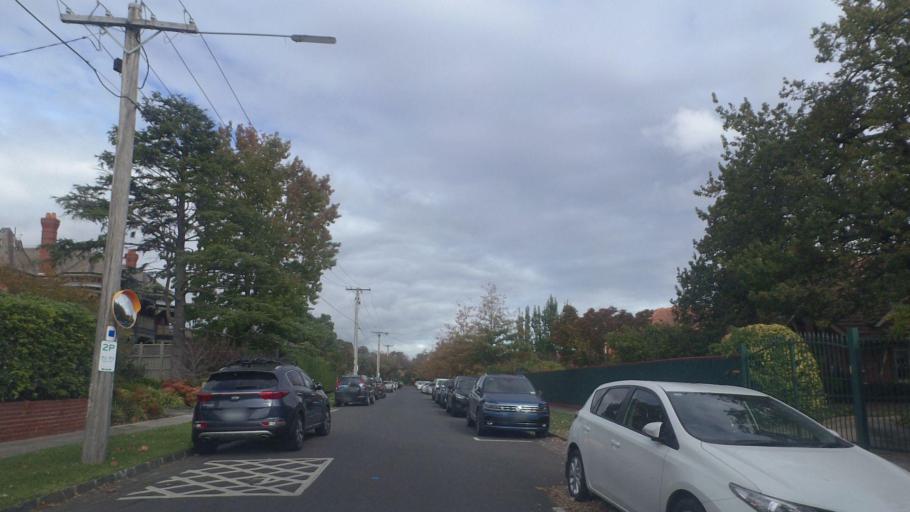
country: AU
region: Victoria
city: Mont Albert
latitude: -37.8195
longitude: 145.1066
